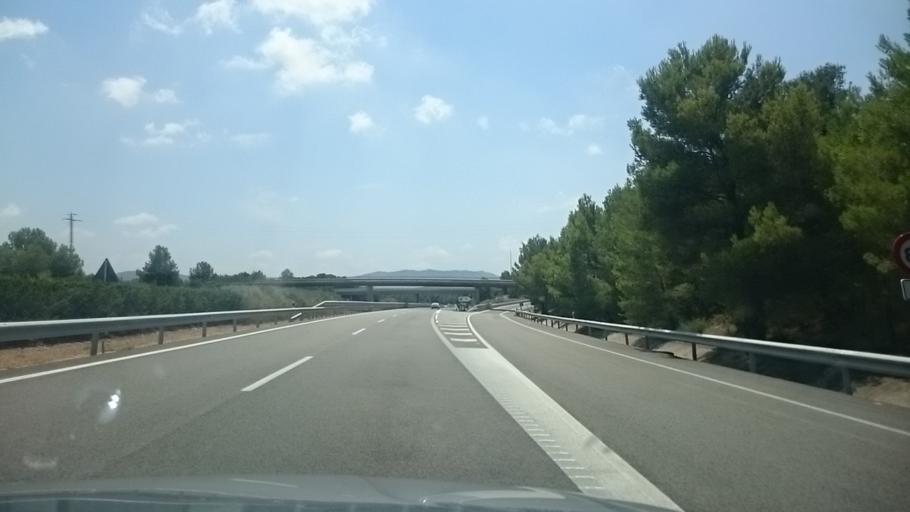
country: ES
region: Catalonia
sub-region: Provincia de Tarragona
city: Alio
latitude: 41.3029
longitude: 1.3465
